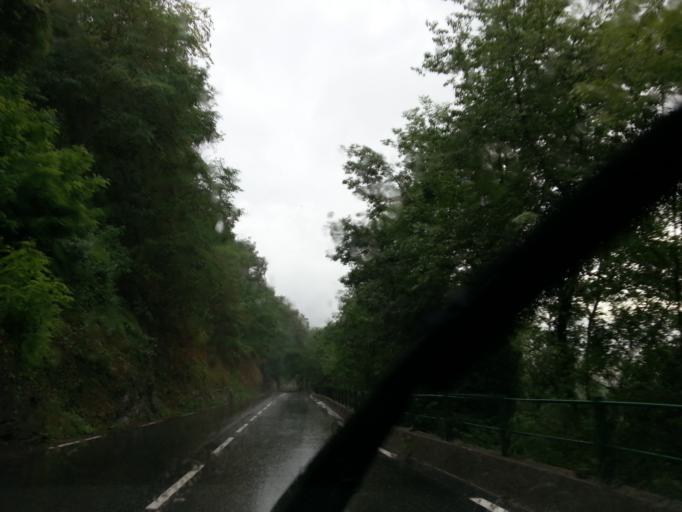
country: FR
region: Rhone-Alpes
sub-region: Departement de la Savoie
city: Albertville
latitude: 45.6813
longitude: 6.3976
